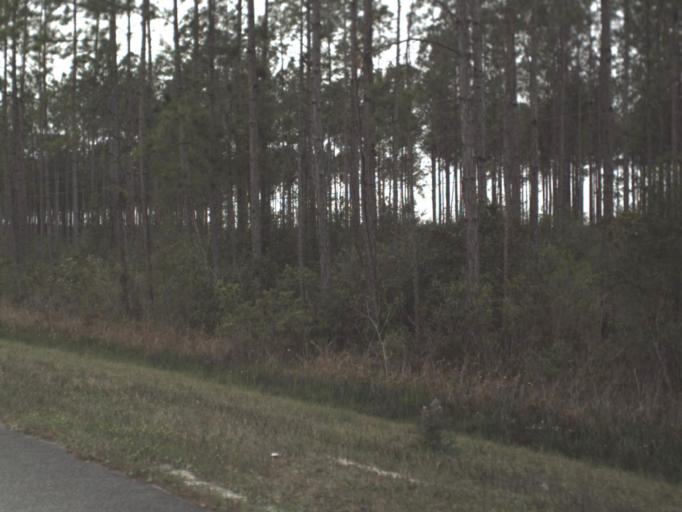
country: US
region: Florida
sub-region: Gulf County
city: Port Saint Joe
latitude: 29.9253
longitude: -85.1964
